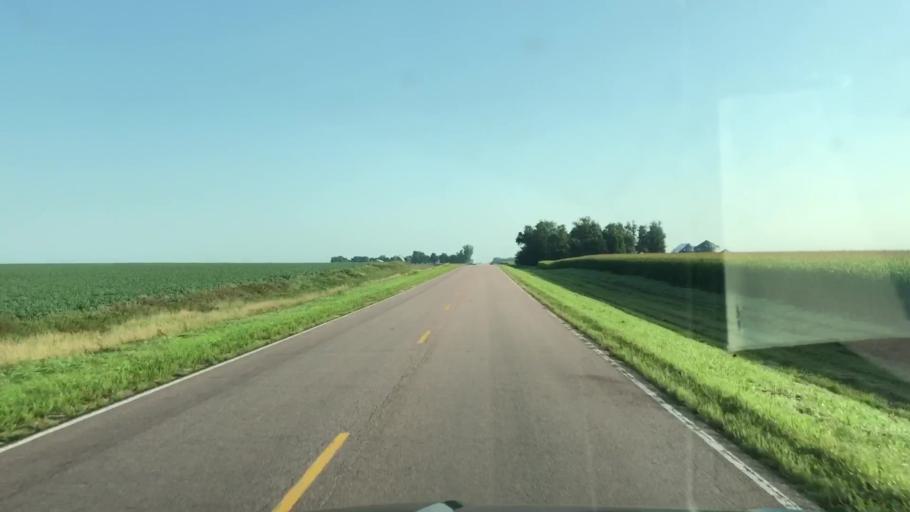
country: US
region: Iowa
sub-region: Lyon County
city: George
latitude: 43.3026
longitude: -95.9993
